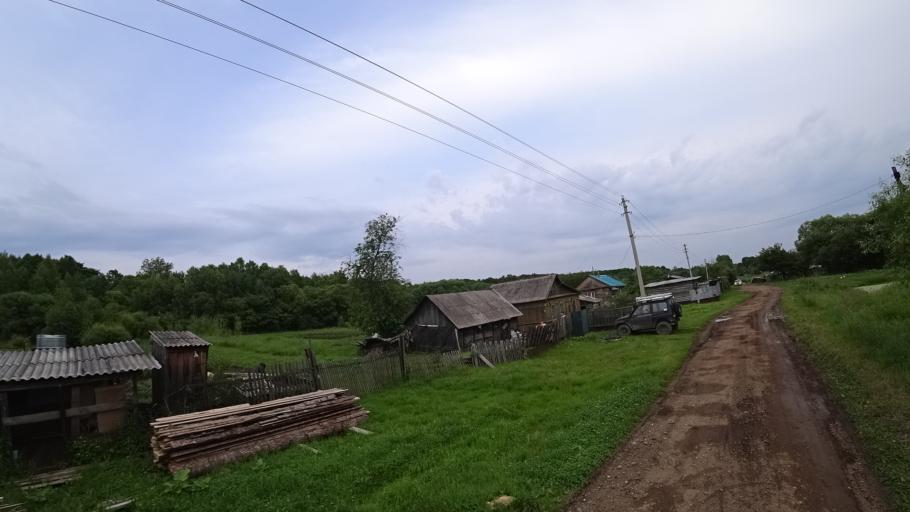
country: RU
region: Primorskiy
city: Novosysoyevka
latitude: 44.2376
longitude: 133.3792
